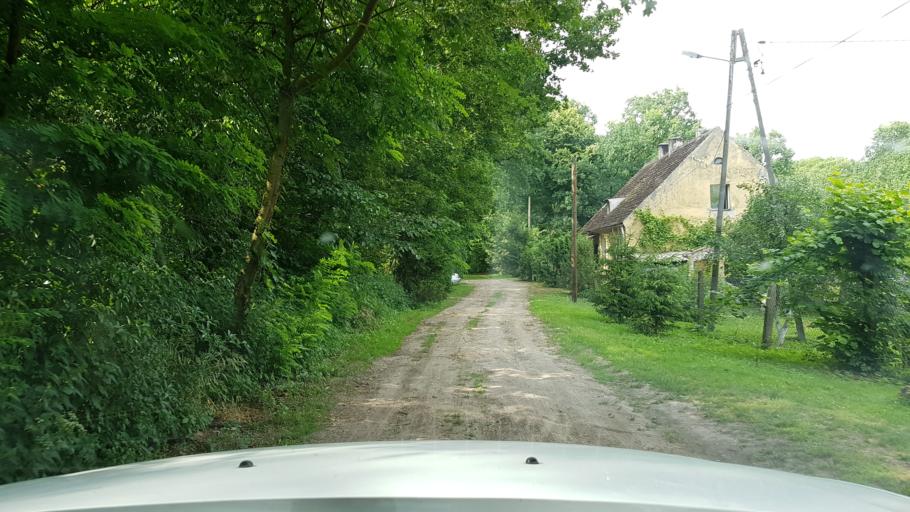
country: PL
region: West Pomeranian Voivodeship
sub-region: Powiat gryfinski
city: Moryn
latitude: 52.9207
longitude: 14.3617
